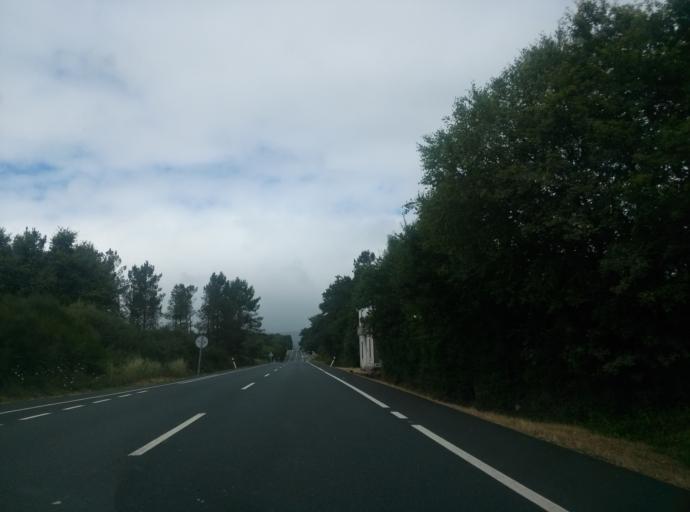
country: ES
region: Galicia
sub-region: Provincia de Lugo
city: Muras
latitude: 43.4031
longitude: -7.7811
